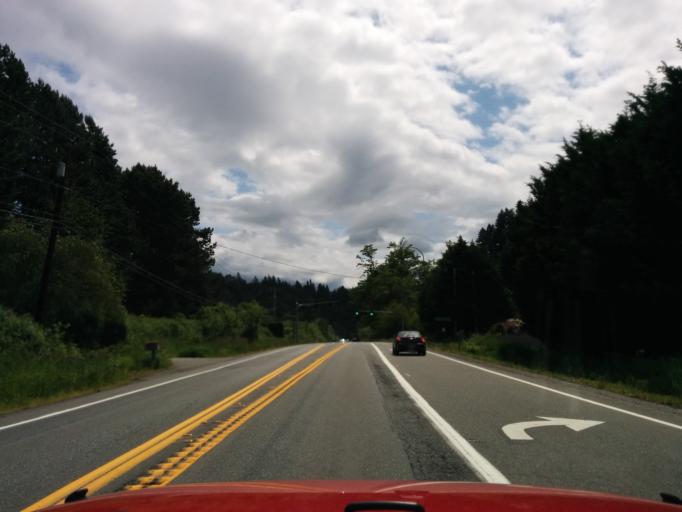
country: US
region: Washington
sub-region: King County
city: Union Hill-Novelty Hill
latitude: 47.6404
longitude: -122.0116
